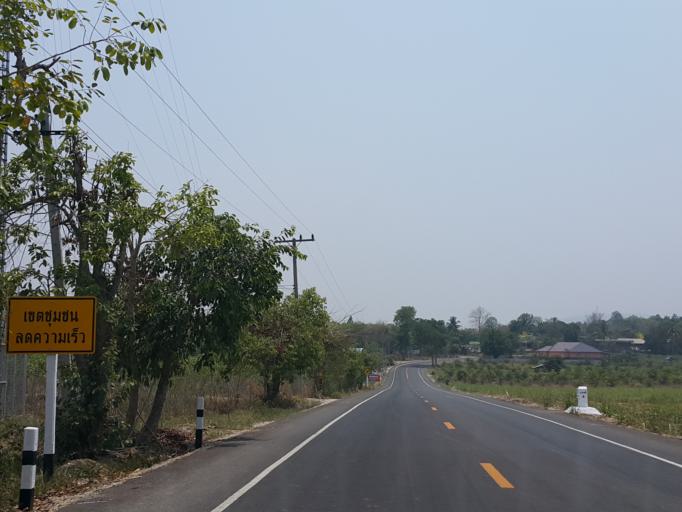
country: TH
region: Kamphaeng Phet
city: Pang Sila Thong
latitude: 16.0311
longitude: 99.3729
